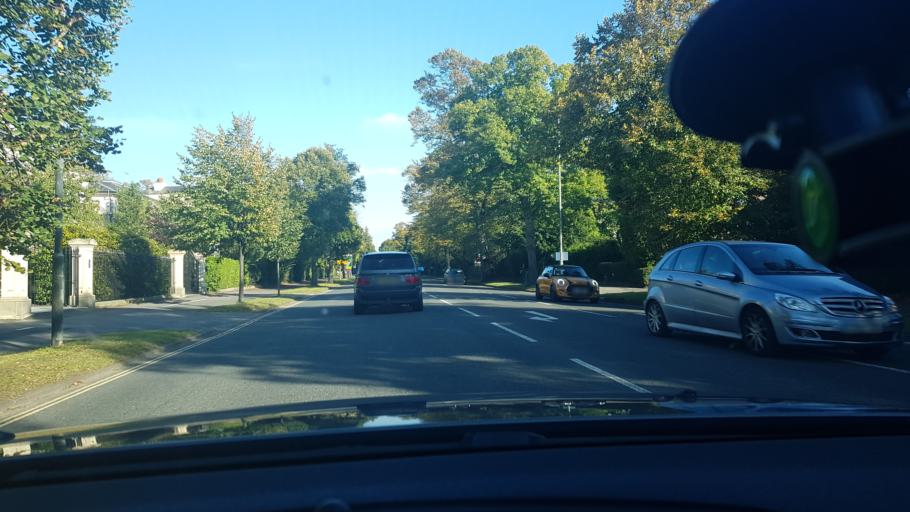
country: GB
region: England
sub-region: Gloucestershire
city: Cheltenham
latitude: 51.8940
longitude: -2.0948
